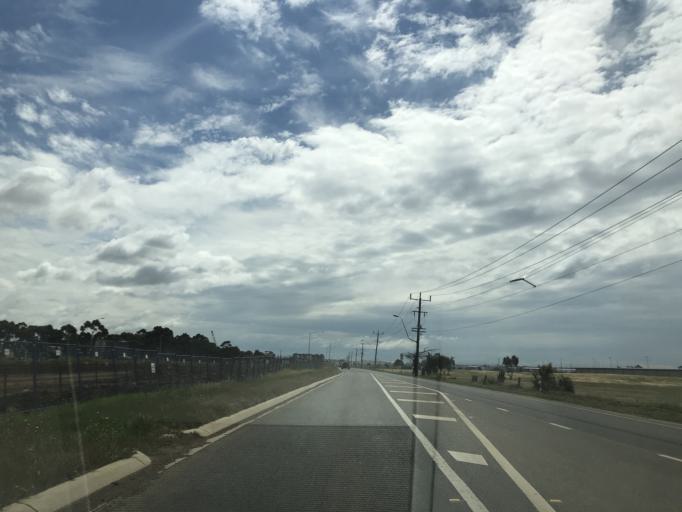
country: AU
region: Victoria
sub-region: Wyndham
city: Truganina
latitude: -37.8308
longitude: 144.7481
